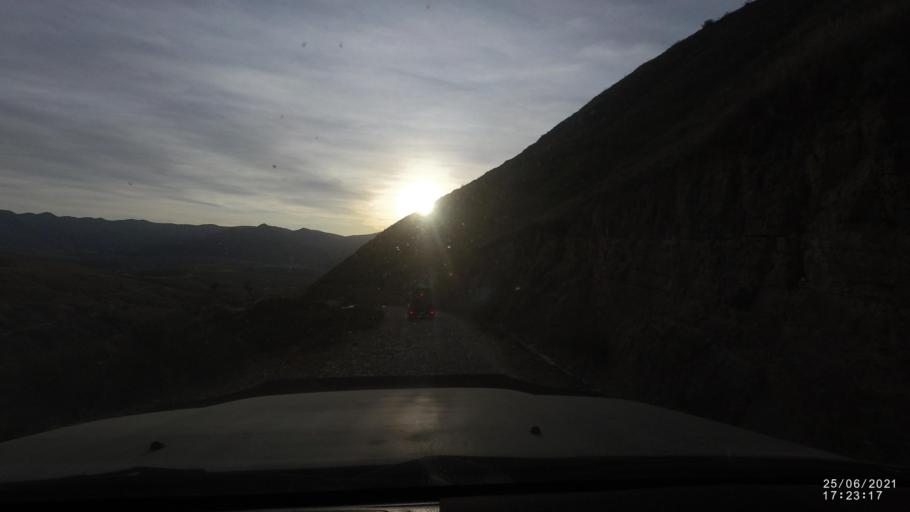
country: BO
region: Cochabamba
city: Mizque
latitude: -17.9119
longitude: -65.6867
